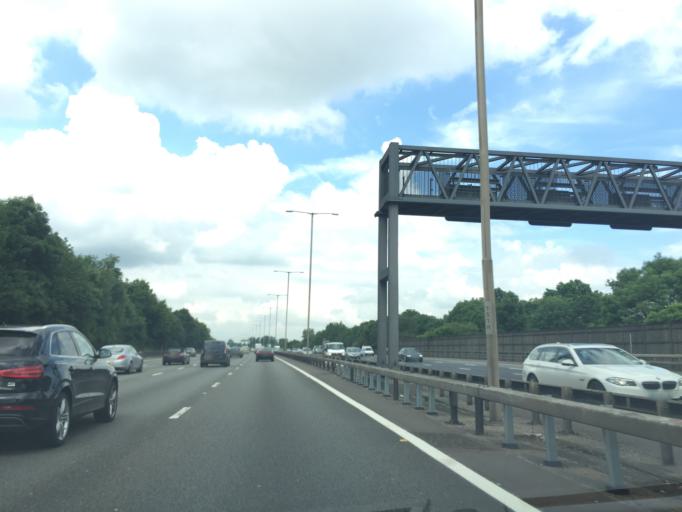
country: GB
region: England
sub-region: Greater London
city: Uxbridge
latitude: 51.5290
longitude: -0.4988
